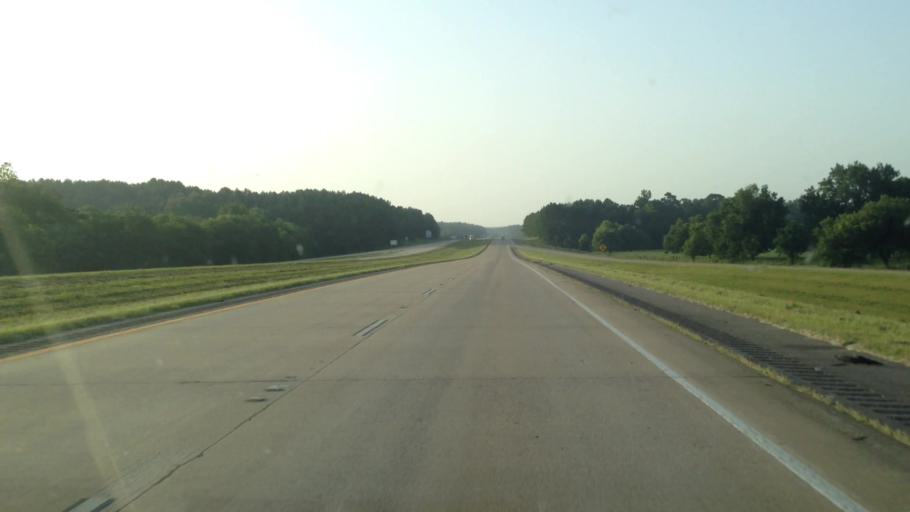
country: US
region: Louisiana
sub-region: Grant Parish
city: Colfax
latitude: 31.4933
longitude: -92.8602
